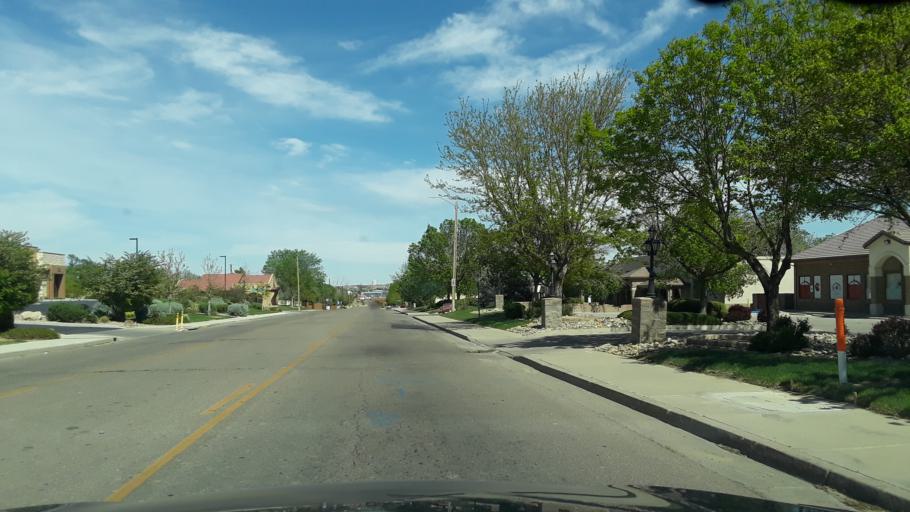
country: US
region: Colorado
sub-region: Pueblo County
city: Pueblo
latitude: 38.3125
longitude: -104.6242
